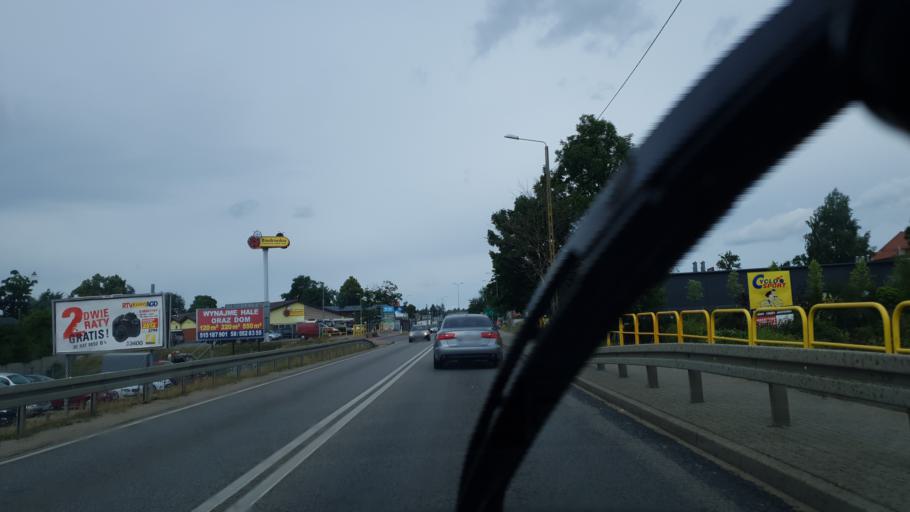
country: PL
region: Pomeranian Voivodeship
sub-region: Powiat kartuski
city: Chwaszczyno
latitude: 54.4420
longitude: 18.4169
